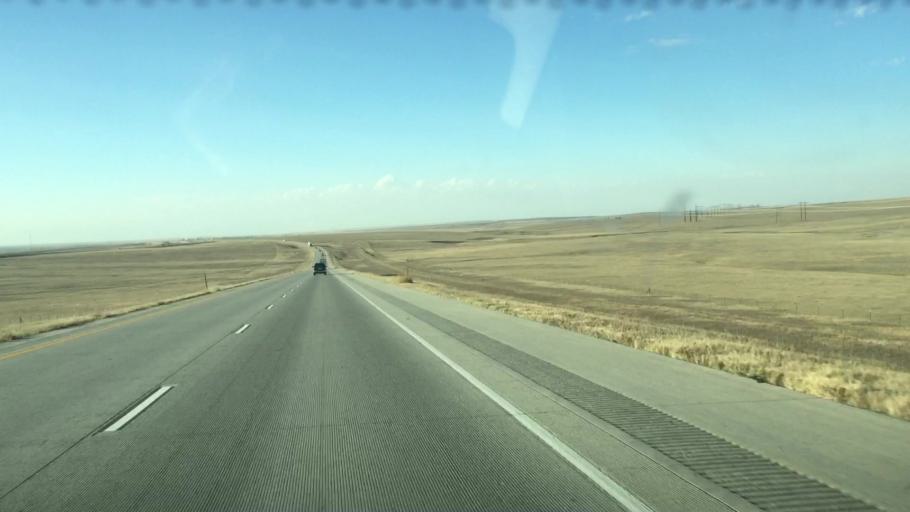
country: US
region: Colorado
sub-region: Lincoln County
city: Limon
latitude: 39.4046
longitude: -103.8961
